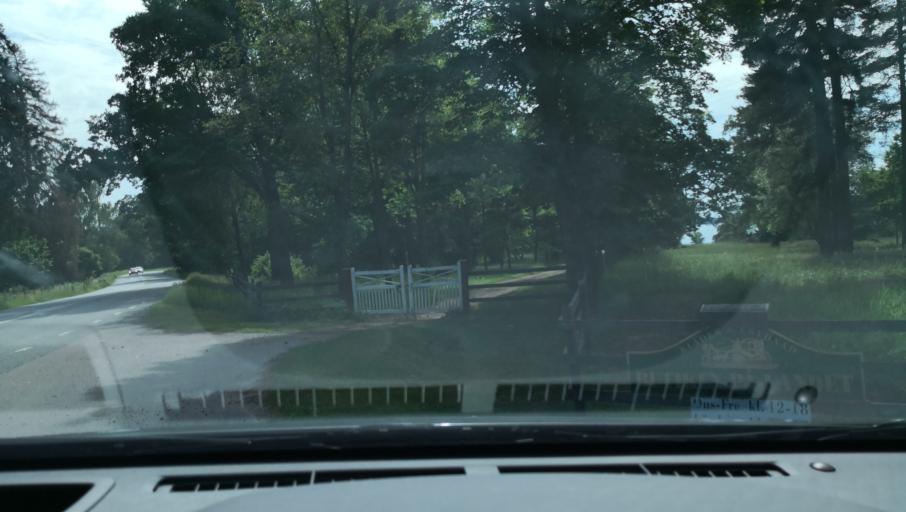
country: SE
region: Uppsala
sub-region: Uppsala Kommun
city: Saevja
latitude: 59.7645
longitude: 17.6461
